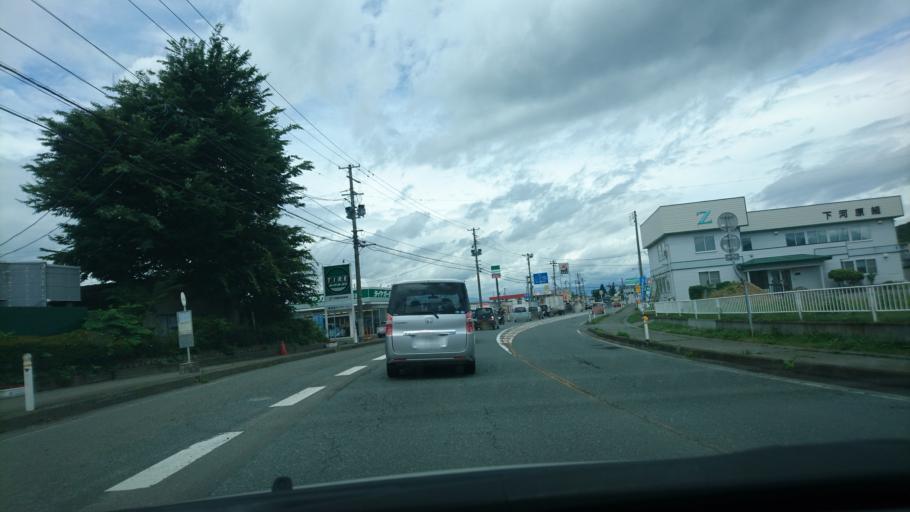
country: JP
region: Iwate
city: Morioka-shi
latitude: 39.6162
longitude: 141.1916
